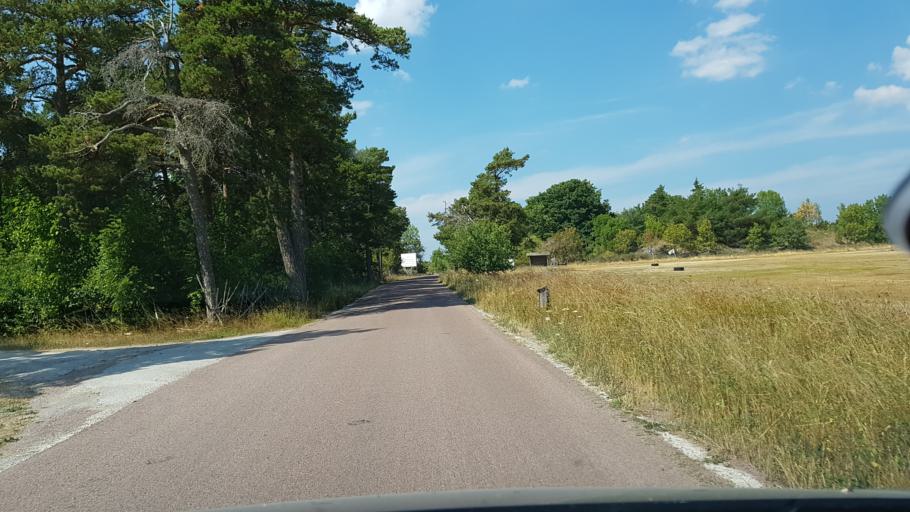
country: SE
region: Gotland
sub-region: Gotland
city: Visby
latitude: 57.6682
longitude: 18.3675
